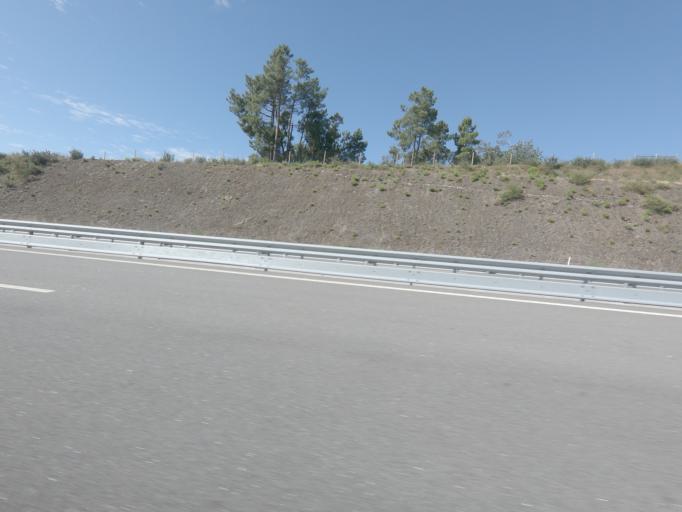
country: PT
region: Vila Real
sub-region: Santa Marta de Penaguiao
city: Santa Marta de Penaguiao
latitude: 41.2664
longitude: -7.8136
